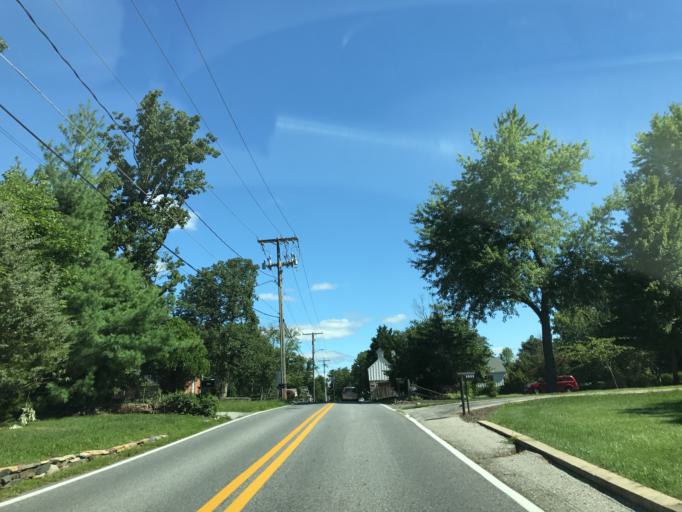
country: US
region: Maryland
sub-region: Howard County
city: Ellicott City
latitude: 39.2790
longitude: -76.7770
